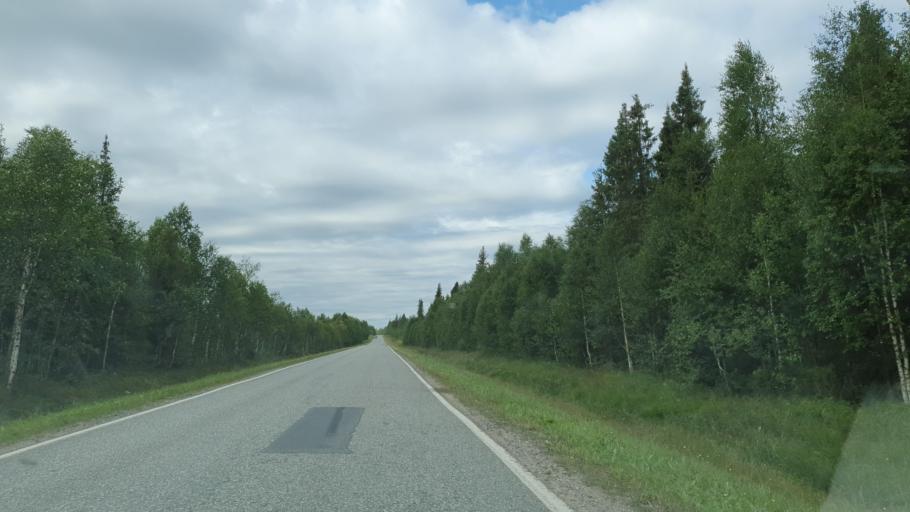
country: FI
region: Lapland
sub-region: Tunturi-Lappi
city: Kittilae
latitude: 67.6156
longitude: 25.3647
